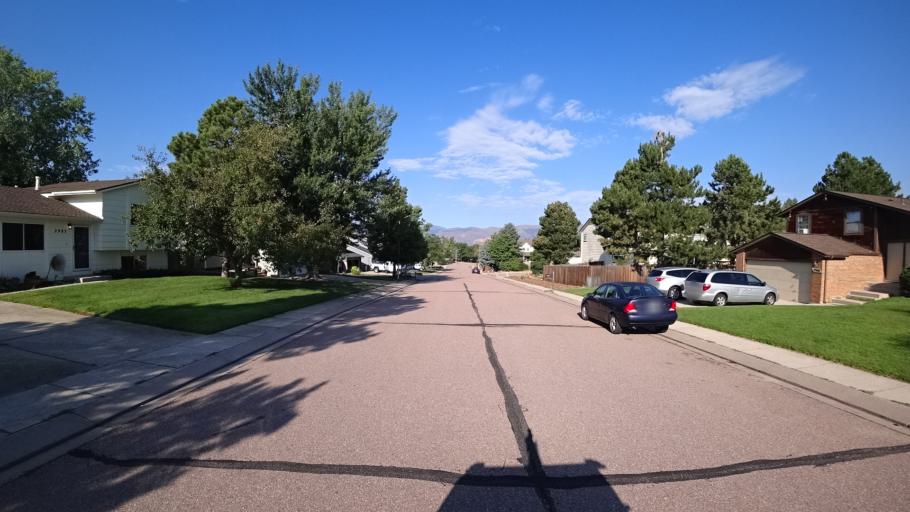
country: US
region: Colorado
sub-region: El Paso County
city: Black Forest
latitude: 38.9451
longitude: -104.7699
